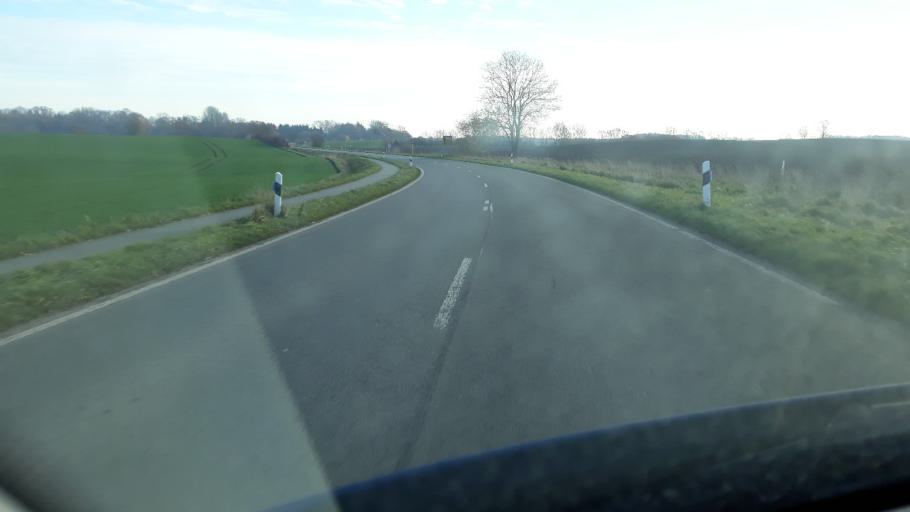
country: DE
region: Schleswig-Holstein
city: Maasholm
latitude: 54.6614
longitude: 9.9775
